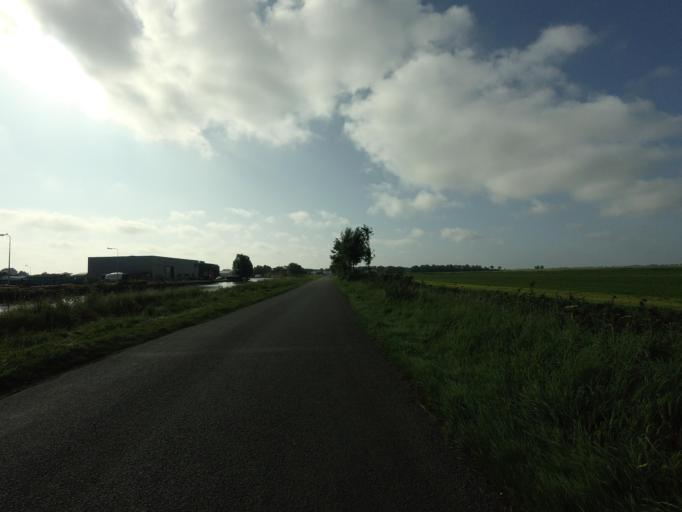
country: NL
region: Overijssel
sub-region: Gemeente Steenwijkerland
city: Tuk
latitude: 52.7804
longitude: 6.0864
